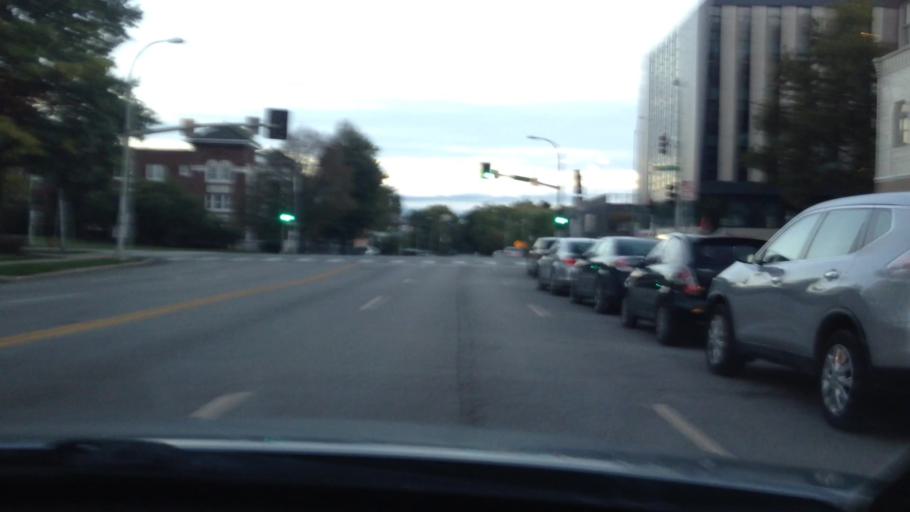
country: US
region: Missouri
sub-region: Jackson County
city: Kansas City
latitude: 39.0642
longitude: -94.5810
